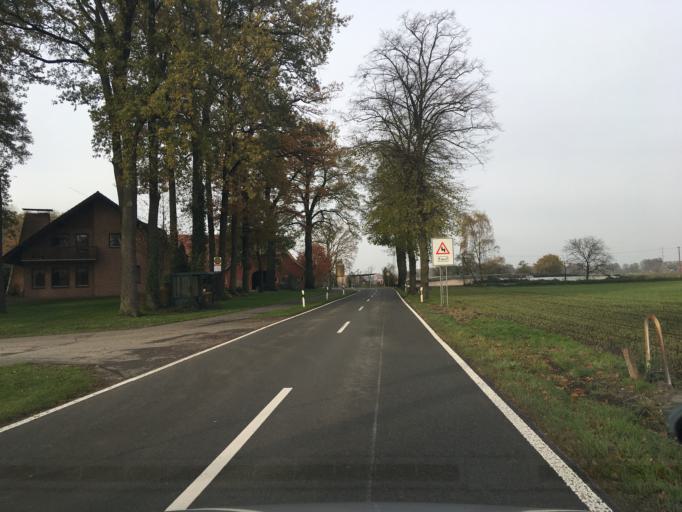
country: DE
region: North Rhine-Westphalia
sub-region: Regierungsbezirk Munster
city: Velen
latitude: 51.9274
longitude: 6.9512
